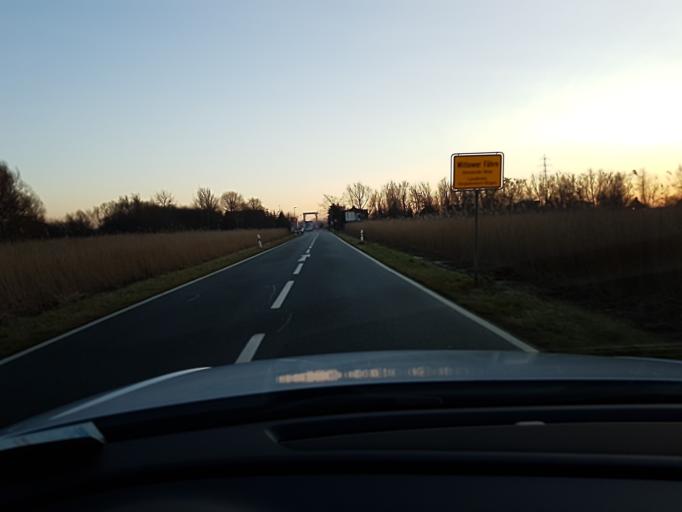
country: DE
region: Mecklenburg-Vorpommern
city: Wiek
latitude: 54.5605
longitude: 13.2475
